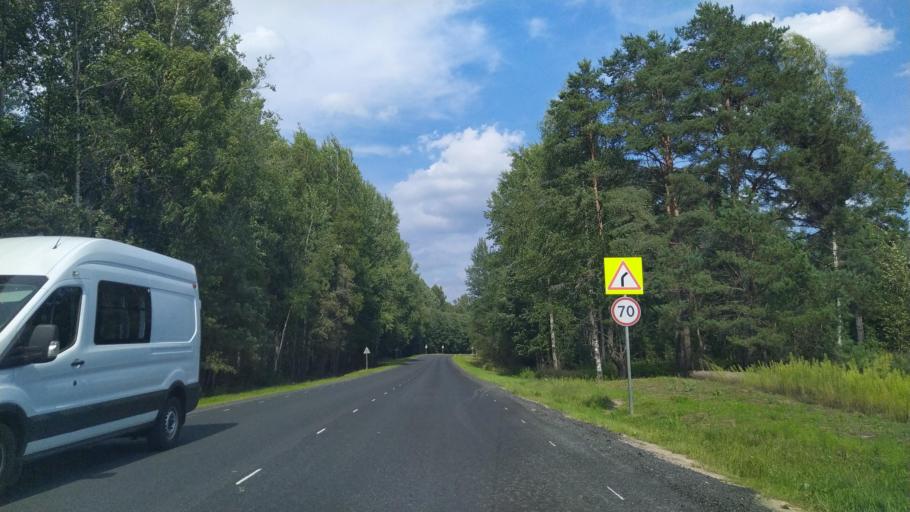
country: RU
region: Pskov
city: Porkhov
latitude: 57.7383
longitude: 29.4177
